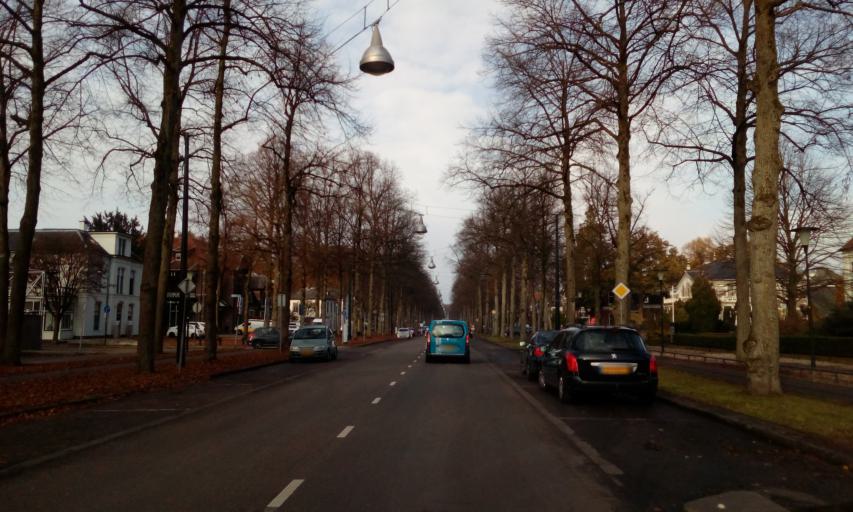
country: NL
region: Gelderland
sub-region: Gemeente Apeldoorn
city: Apeldoorn
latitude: 52.2215
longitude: 5.9541
